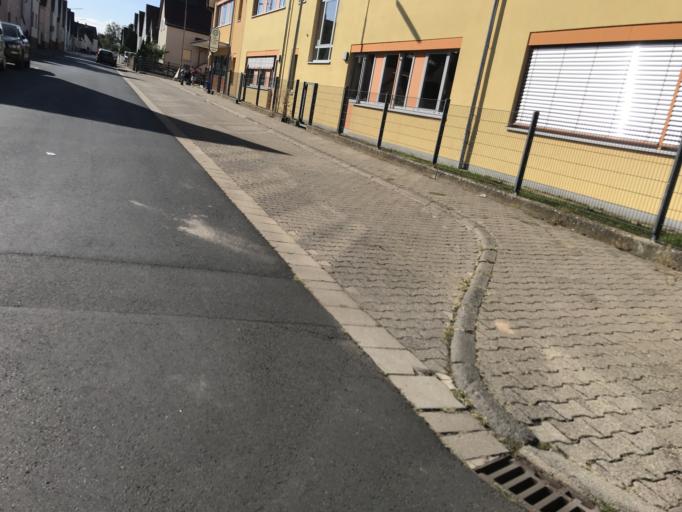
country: DE
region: Hesse
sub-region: Regierungsbezirk Darmstadt
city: Glauburg
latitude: 50.2915
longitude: 8.9842
